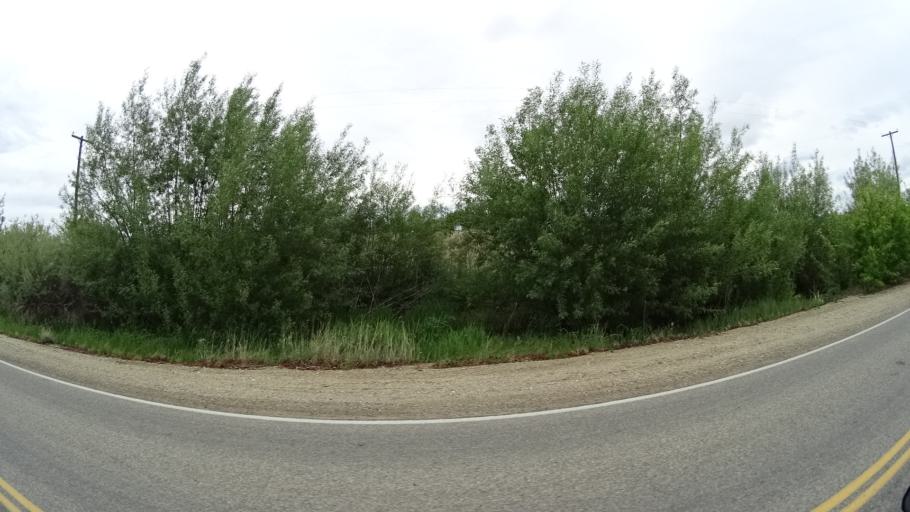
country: US
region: Idaho
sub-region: Ada County
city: Star
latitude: 43.7094
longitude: -116.4684
